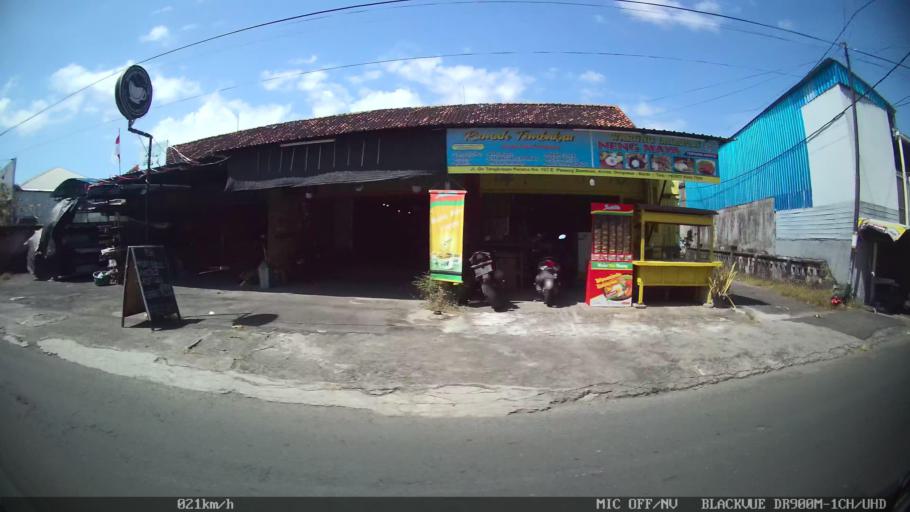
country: ID
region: Bali
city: Denpasar
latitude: -8.6681
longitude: 115.1820
